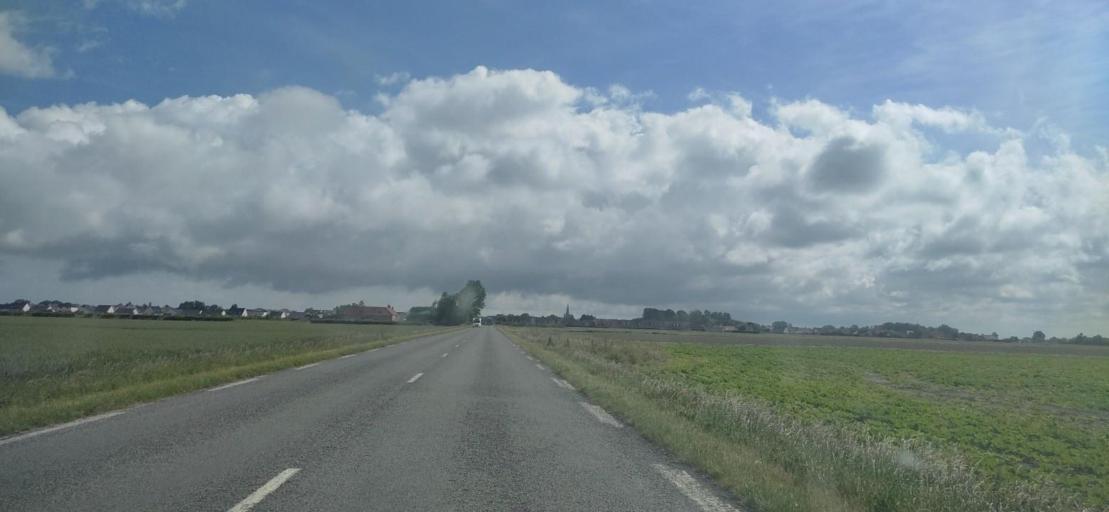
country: FR
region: Nord-Pas-de-Calais
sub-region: Departement du Pas-de-Calais
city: Oye-Plage
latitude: 50.9721
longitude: 2.0257
